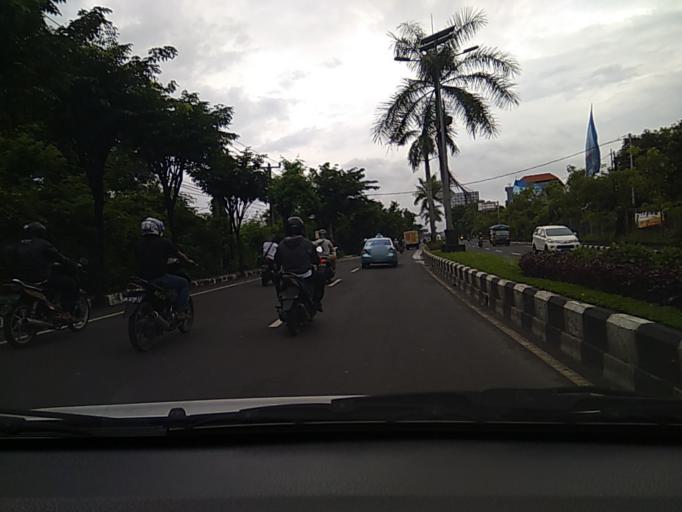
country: ID
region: Bali
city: Jimbaran
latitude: -8.7795
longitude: 115.1777
